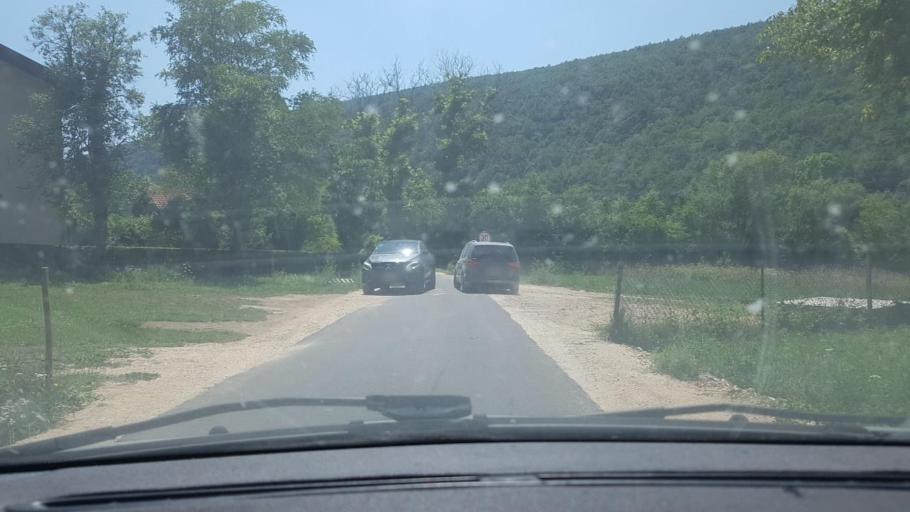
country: BA
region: Federation of Bosnia and Herzegovina
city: Orasac
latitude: 44.6391
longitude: 16.0426
